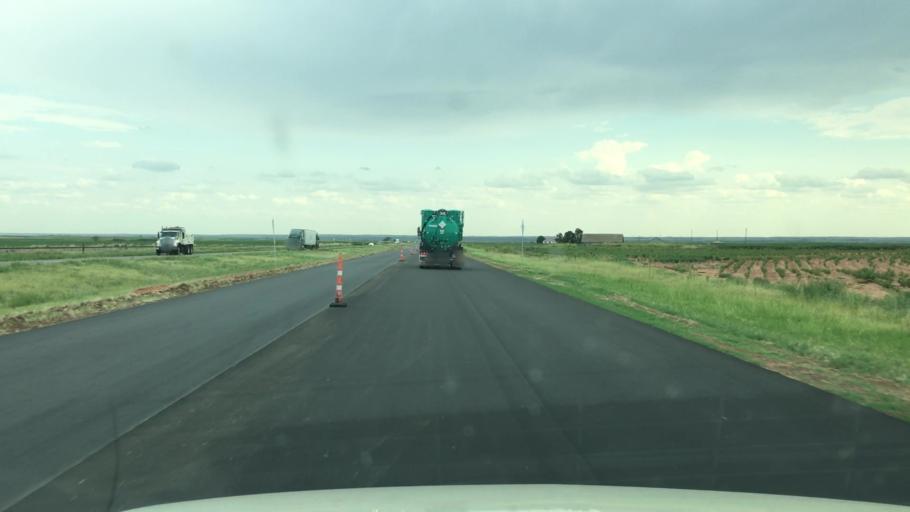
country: US
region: Texas
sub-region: Hall County
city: Memphis
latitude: 34.6227
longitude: -100.4731
